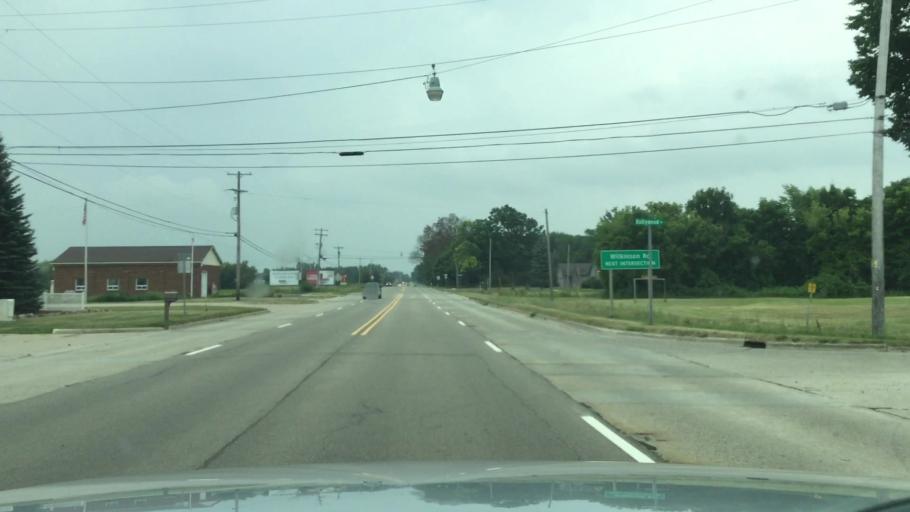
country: US
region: Michigan
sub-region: Shiawassee County
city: Owosso
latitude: 43.0280
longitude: -84.1769
